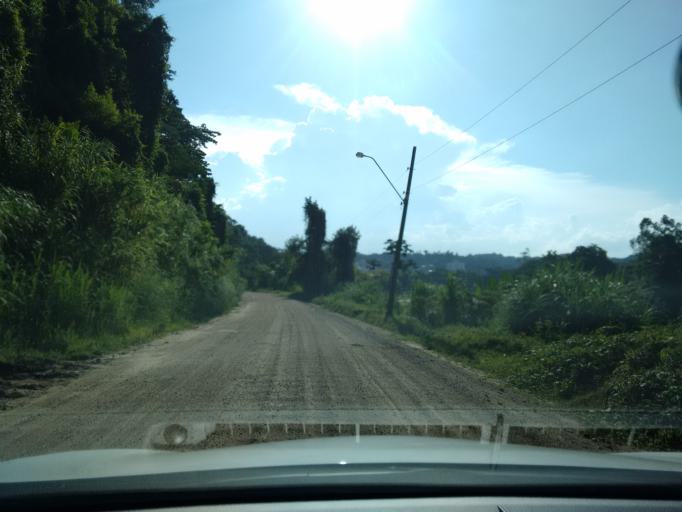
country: BR
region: Santa Catarina
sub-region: Blumenau
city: Blumenau
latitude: -26.8982
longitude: -49.0700
